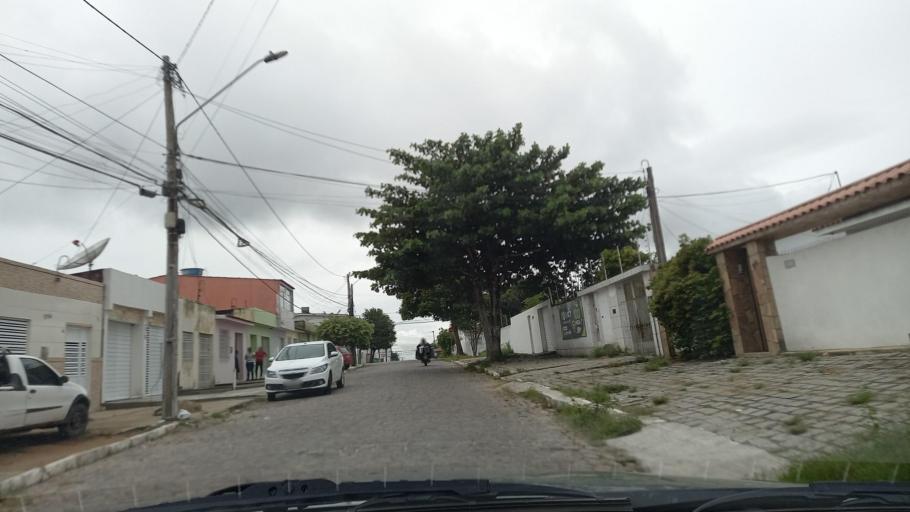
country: BR
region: Pernambuco
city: Garanhuns
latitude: -8.8814
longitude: -36.4830
